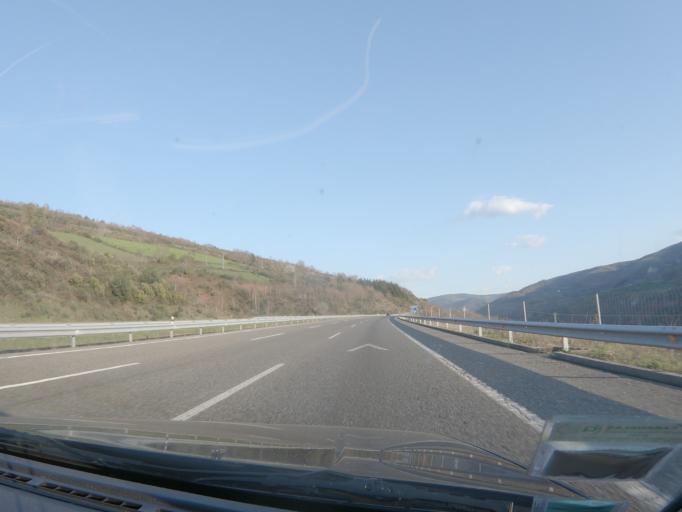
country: ES
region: Galicia
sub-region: Provincia de Lugo
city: San Roman
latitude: 42.7723
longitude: -7.0925
